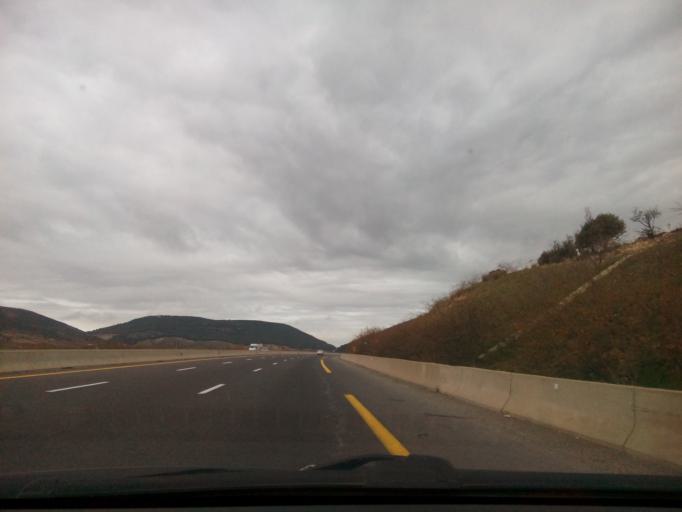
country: DZ
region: Sidi Bel Abbes
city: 'Ain el Berd
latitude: 35.3623
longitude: -0.5057
